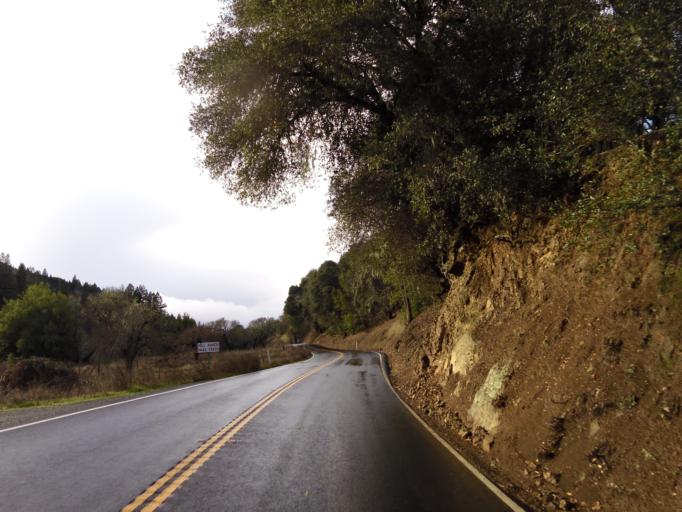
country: US
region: California
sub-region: Sonoma County
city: Cloverdale
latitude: 38.8860
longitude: -123.1616
